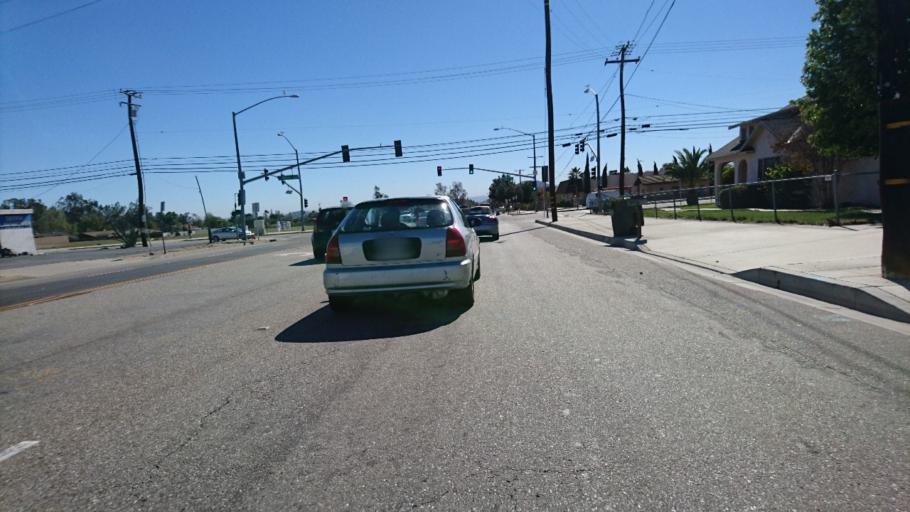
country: US
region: California
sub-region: San Bernardino County
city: Fontana
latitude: 34.1145
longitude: -117.4359
